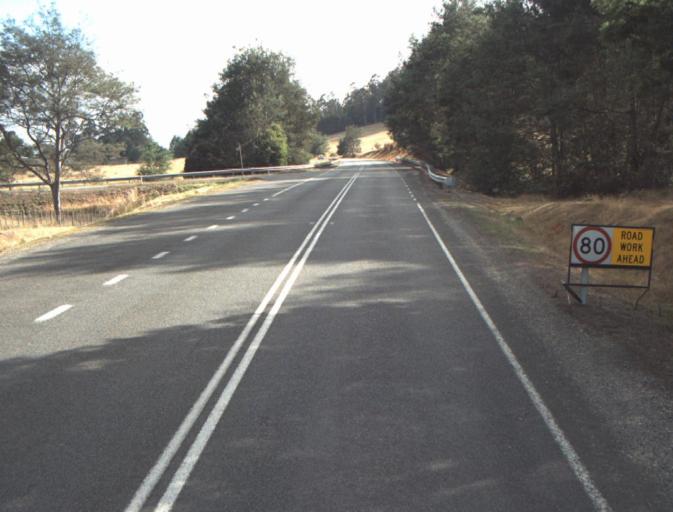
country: AU
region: Tasmania
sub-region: Launceston
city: Mayfield
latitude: -41.2929
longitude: 147.2155
